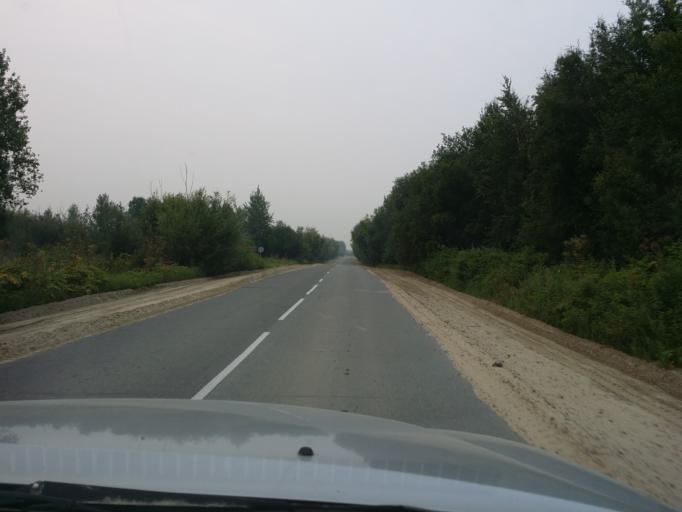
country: RU
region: Khanty-Mansiyskiy Avtonomnyy Okrug
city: Megion
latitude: 61.0087
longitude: 76.3120
